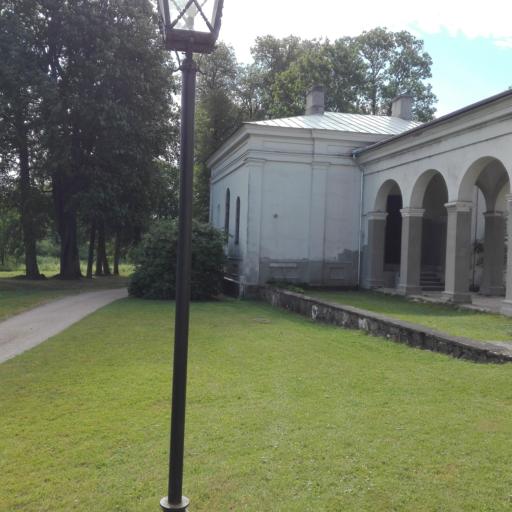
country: LT
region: Panevezys
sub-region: Birzai
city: Birzai
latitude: 56.2195
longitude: 24.7688
